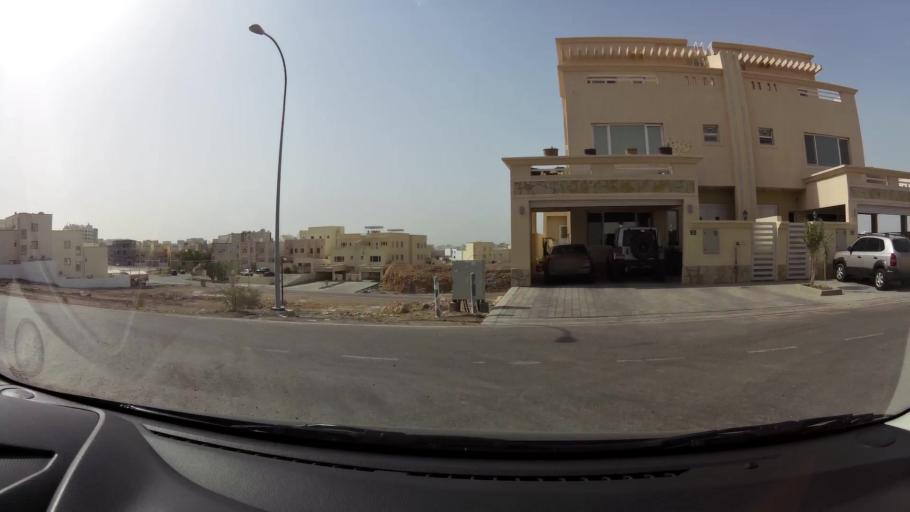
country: OM
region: Muhafazat Masqat
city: Bawshar
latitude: 23.5502
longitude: 58.3504
